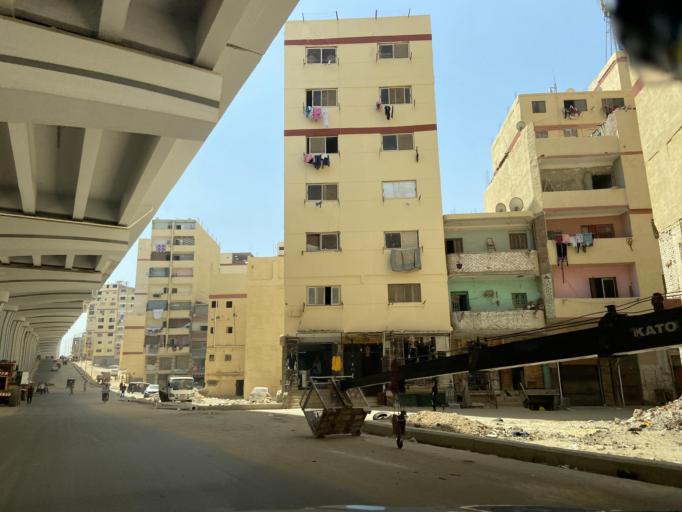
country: EG
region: Muhafazat al Qahirah
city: Cairo
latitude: 30.0652
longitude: 31.3824
